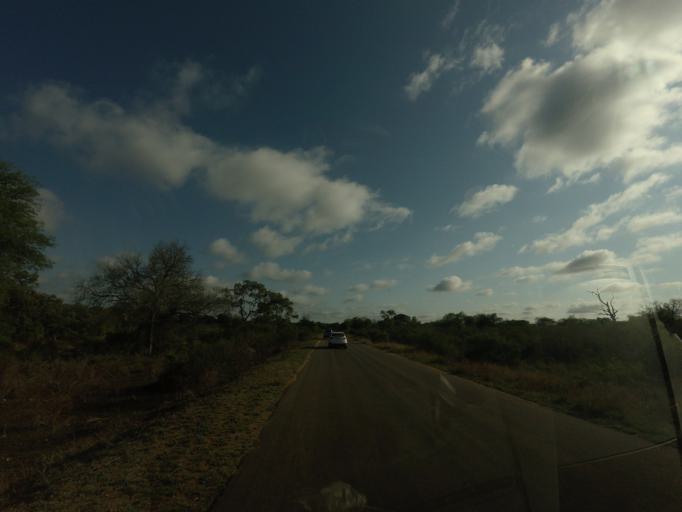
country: ZA
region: Mpumalanga
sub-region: Ehlanzeni District
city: Komatipoort
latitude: -25.2495
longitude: 31.8481
